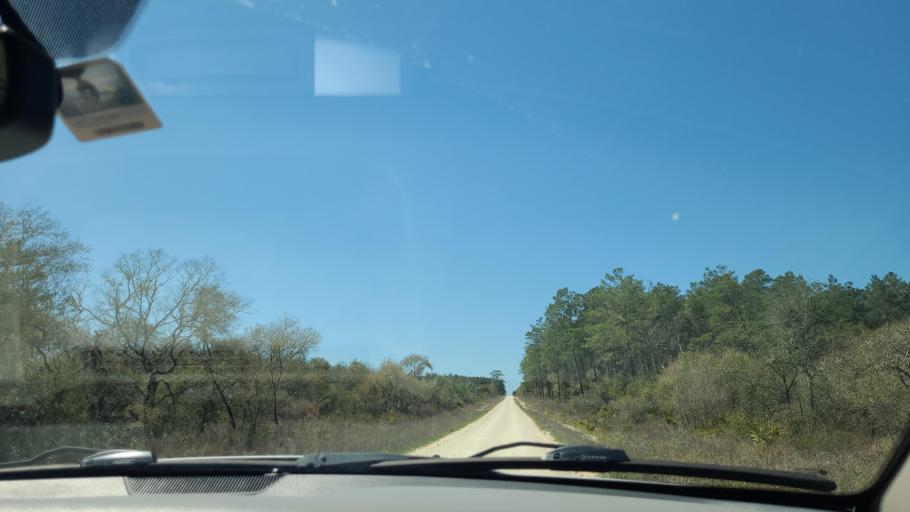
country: US
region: Florida
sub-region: Putnam County
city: Interlachen
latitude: 29.4288
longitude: -81.8181
